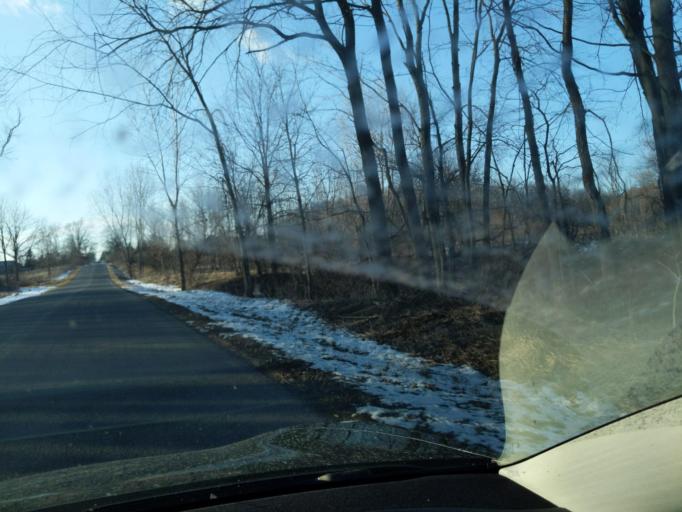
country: US
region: Michigan
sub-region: Ingham County
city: Stockbridge
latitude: 42.5208
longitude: -84.2474
